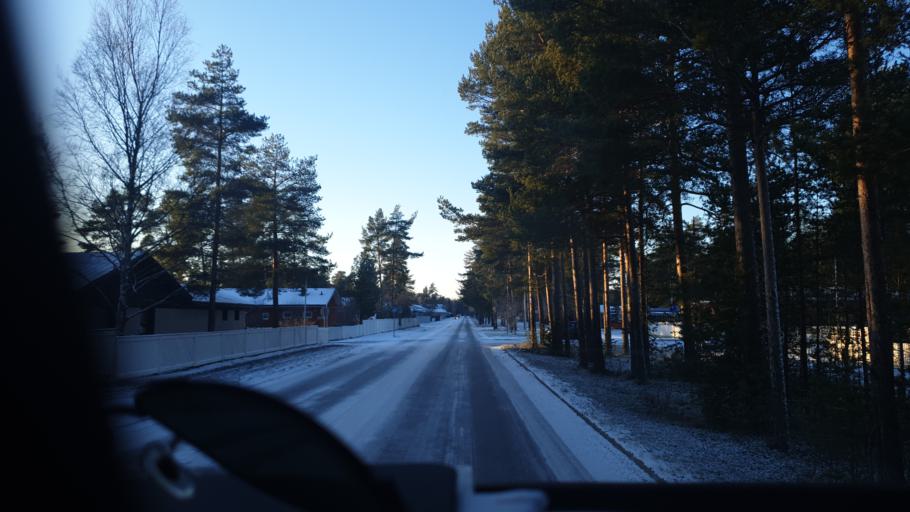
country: FI
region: Central Ostrobothnia
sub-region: Kokkola
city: Kokkola
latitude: 63.8254
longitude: 23.0865
